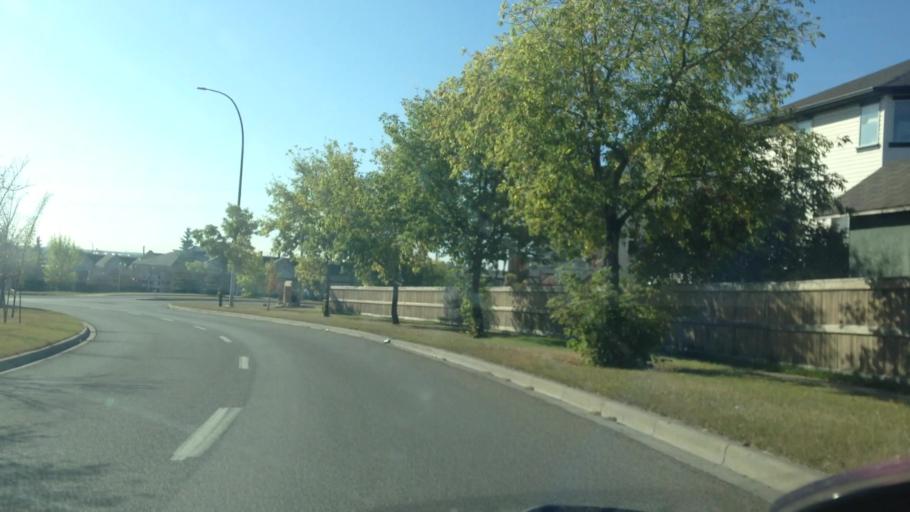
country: CA
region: Alberta
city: Calgary
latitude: 51.1443
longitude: -114.0729
